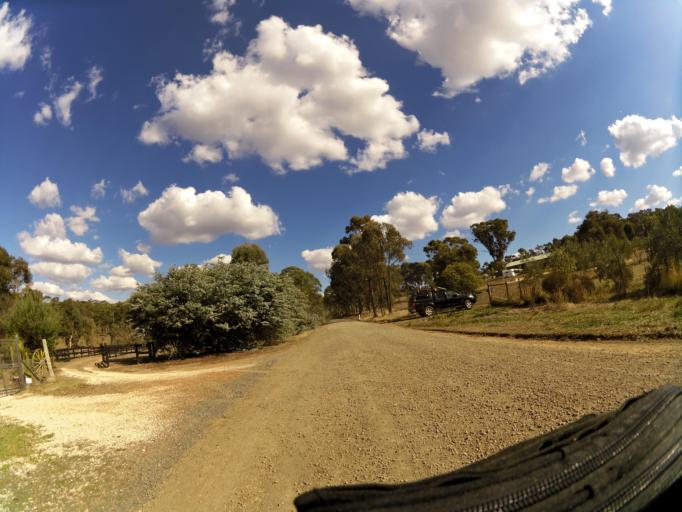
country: AU
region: Victoria
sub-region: Greater Bendigo
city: Kennington
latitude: -36.9579
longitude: 144.7810
